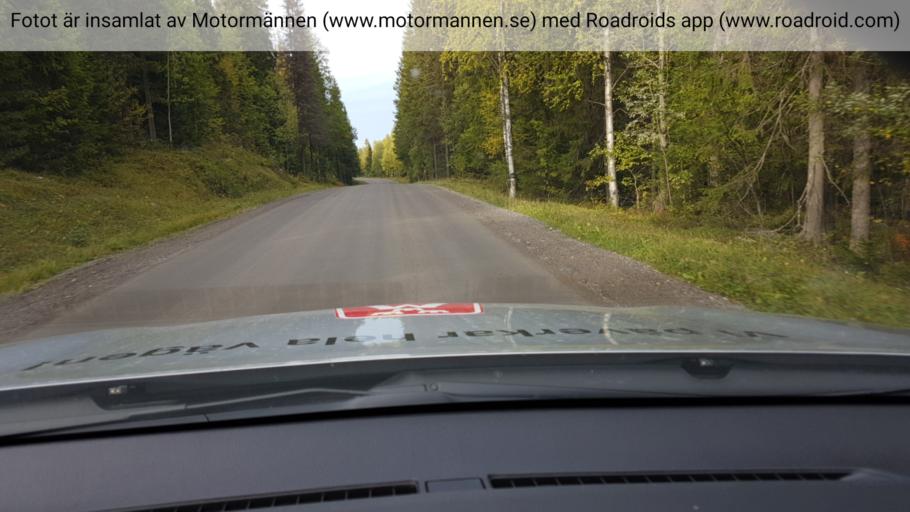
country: SE
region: Jaemtland
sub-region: Stroemsunds Kommun
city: Stroemsund
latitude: 64.0002
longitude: 15.8165
